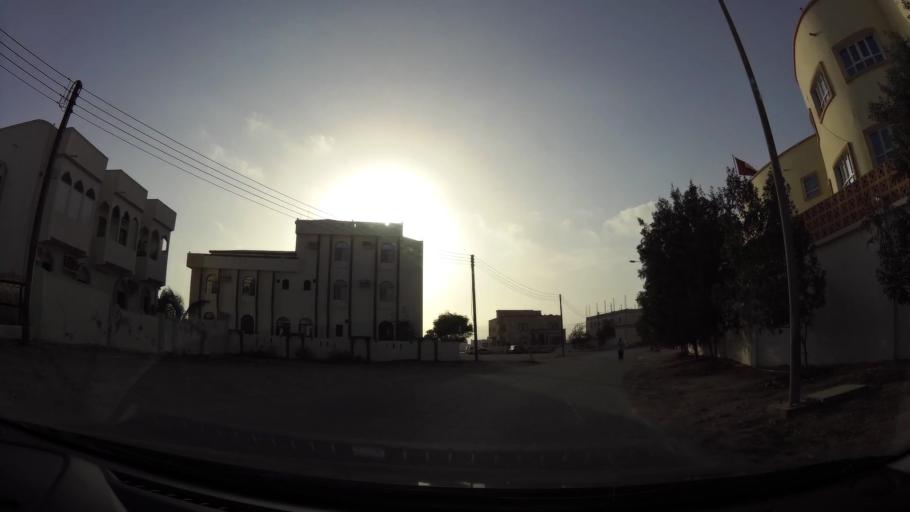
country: OM
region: Zufar
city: Salalah
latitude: 16.9953
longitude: 54.0268
